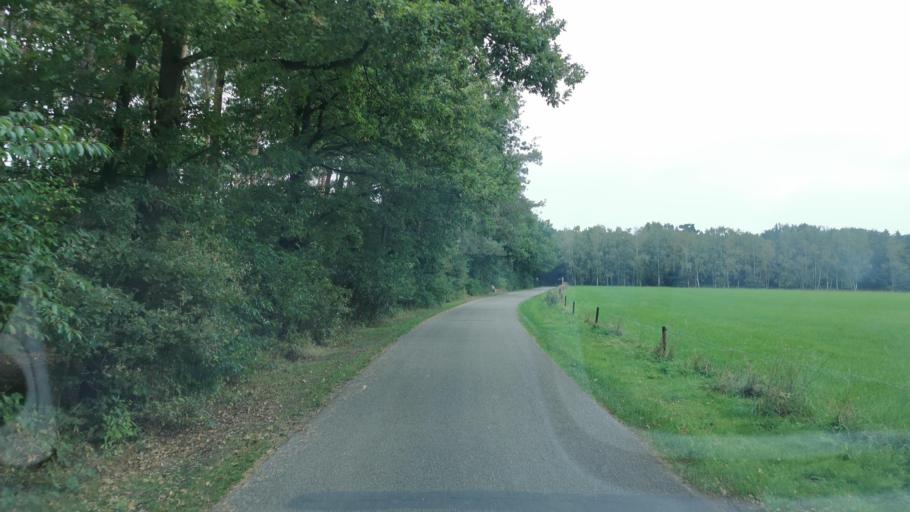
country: NL
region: Overijssel
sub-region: Gemeente Losser
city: Losser
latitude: 52.3196
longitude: 7.0302
